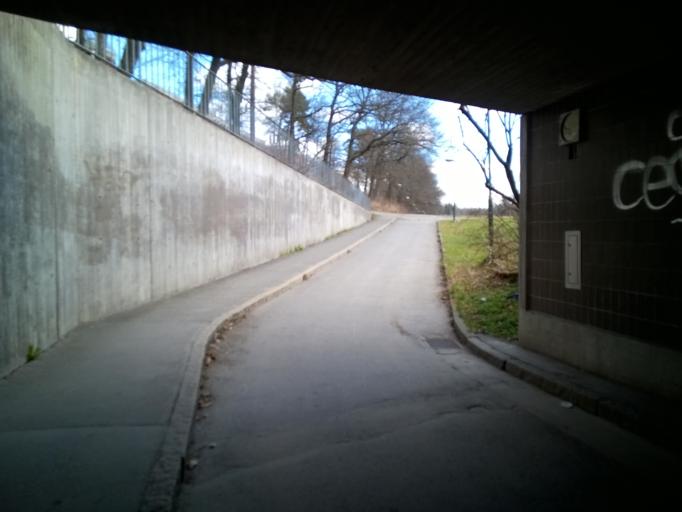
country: SE
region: Stockholm
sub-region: Norrtalje Kommun
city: Bergshamra
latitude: 59.3697
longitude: 18.0606
